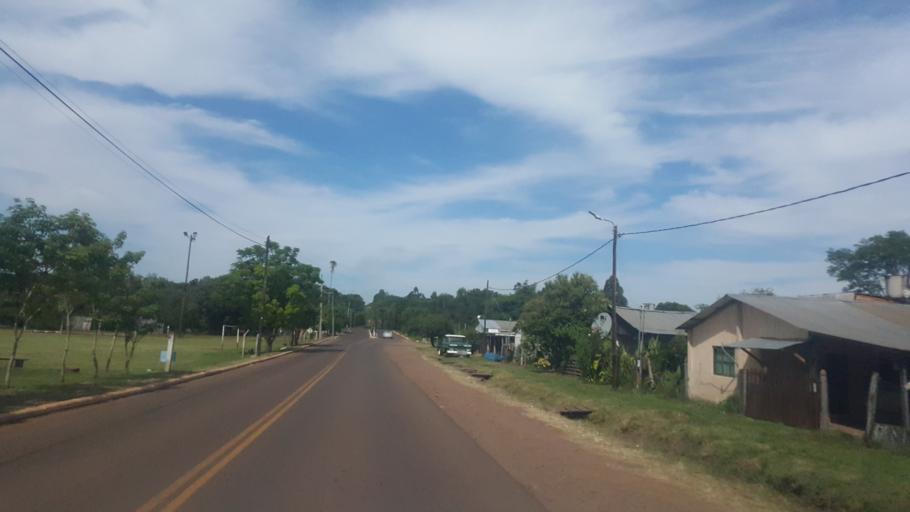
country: AR
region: Misiones
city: Cerro Cora
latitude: -27.5114
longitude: -55.6076
